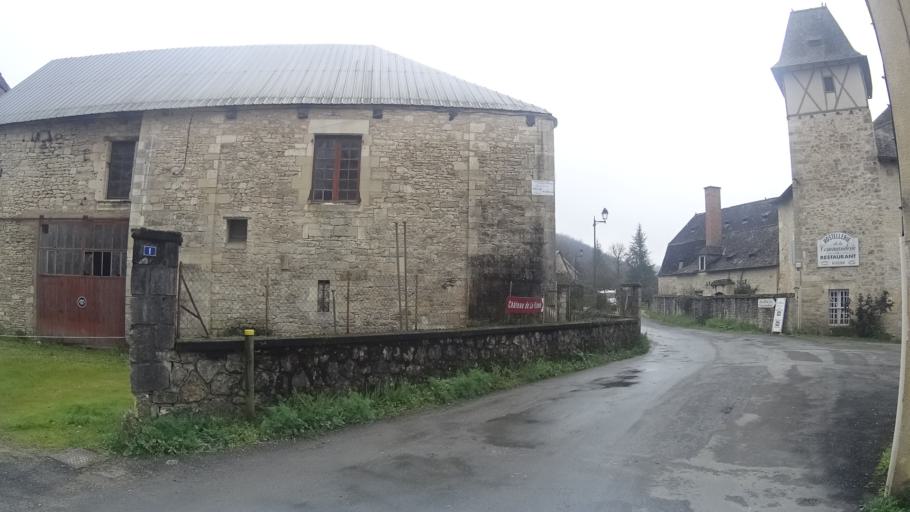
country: FR
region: Aquitaine
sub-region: Departement de la Dordogne
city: Terrasson-Lavilledieu
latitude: 45.1170
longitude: 1.2285
